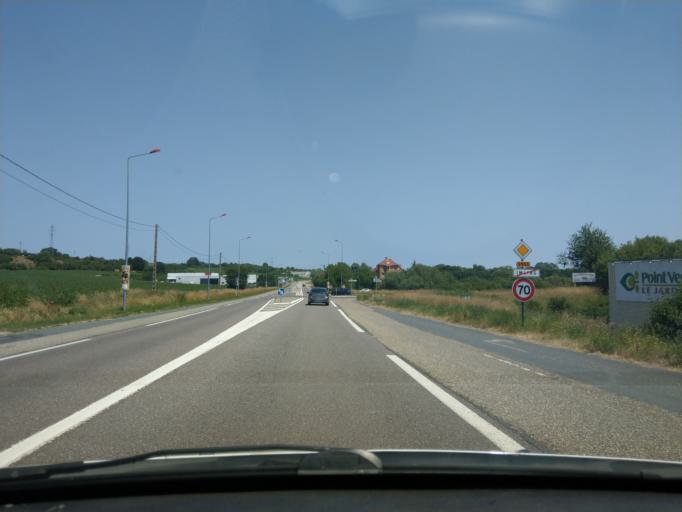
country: FR
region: Lorraine
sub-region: Departement de la Moselle
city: Sarrebourg
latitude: 48.7233
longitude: 7.0187
